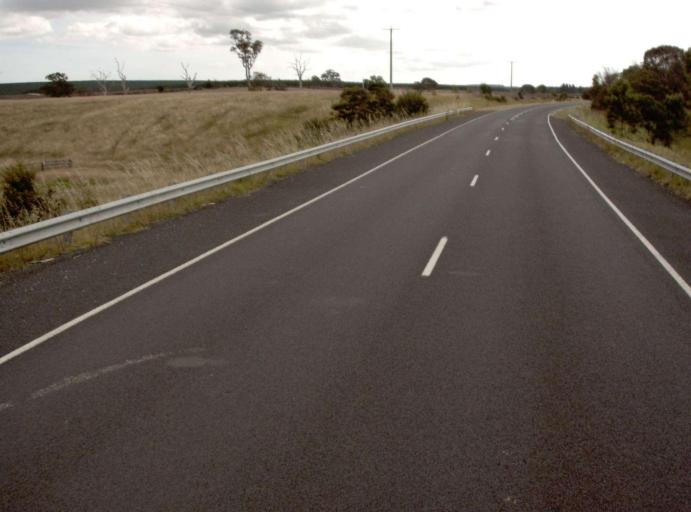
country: AU
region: Victoria
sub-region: Wellington
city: Sale
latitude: -38.1654
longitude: 147.0674
